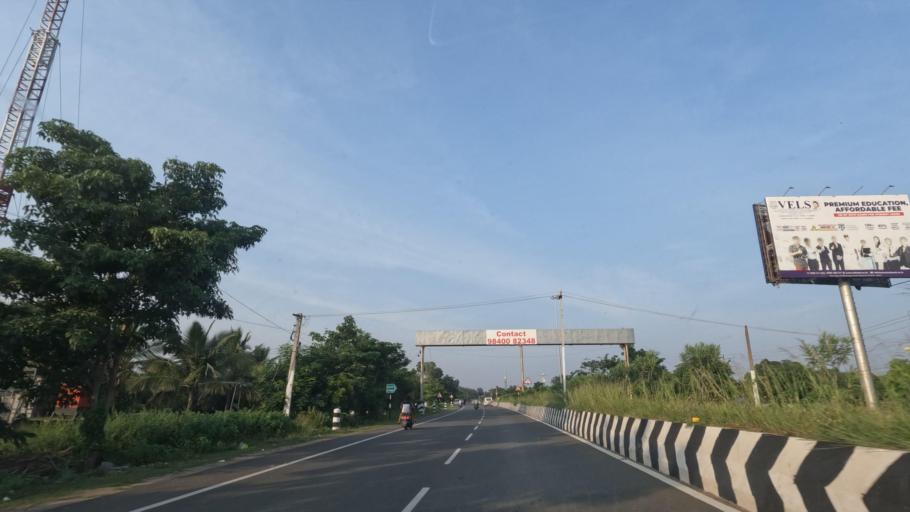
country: IN
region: Tamil Nadu
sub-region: Kancheepuram
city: Mamallapuram
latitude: 12.6478
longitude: 80.2029
